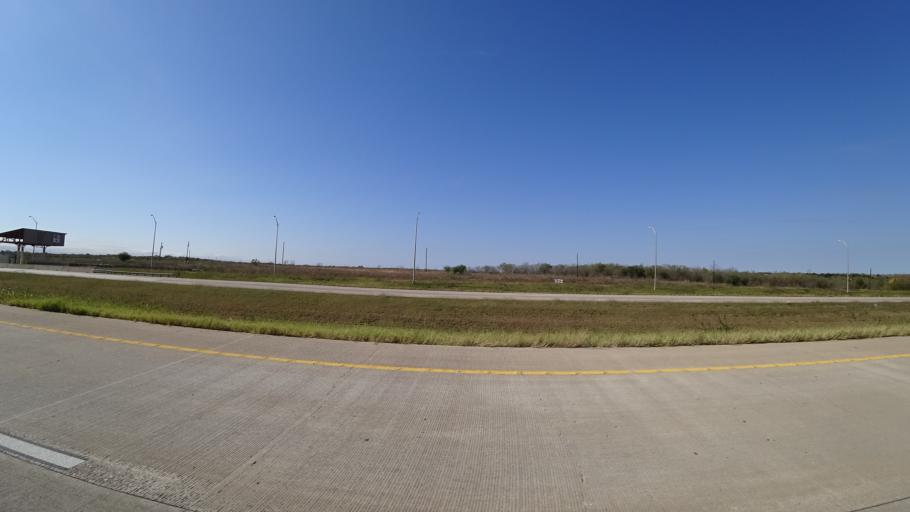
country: US
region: Texas
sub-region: Travis County
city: Onion Creek
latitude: 30.1348
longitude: -97.6661
